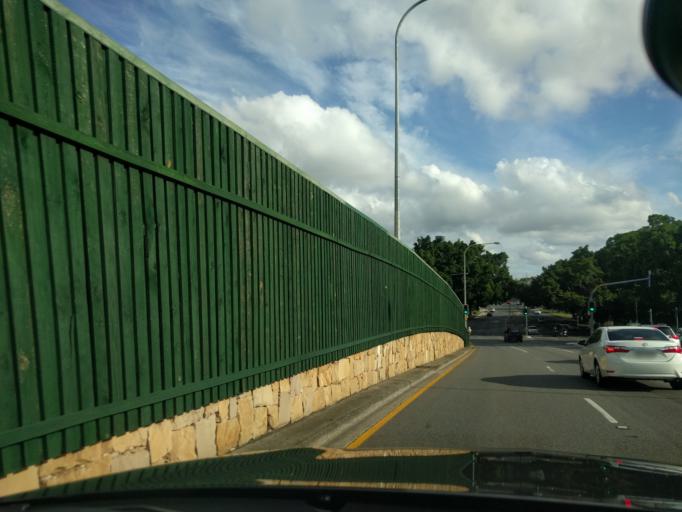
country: AU
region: Queensland
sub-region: Brisbane
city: Spring Hill
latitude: -27.4527
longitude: 153.0114
